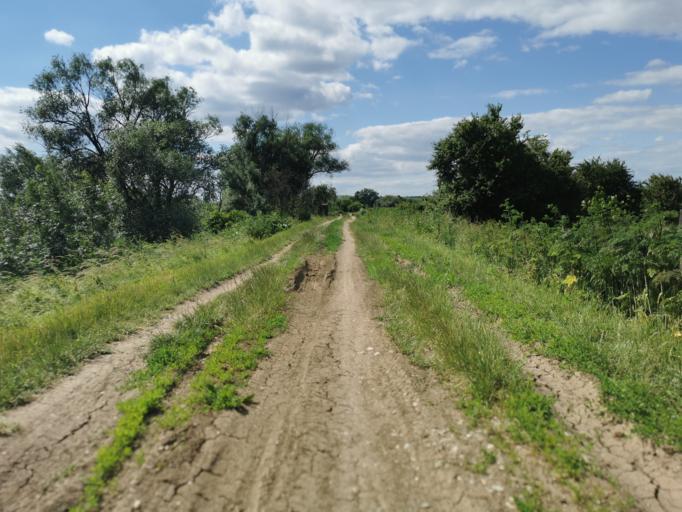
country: CZ
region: South Moravian
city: Rohatec
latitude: 48.8756
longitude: 17.2077
